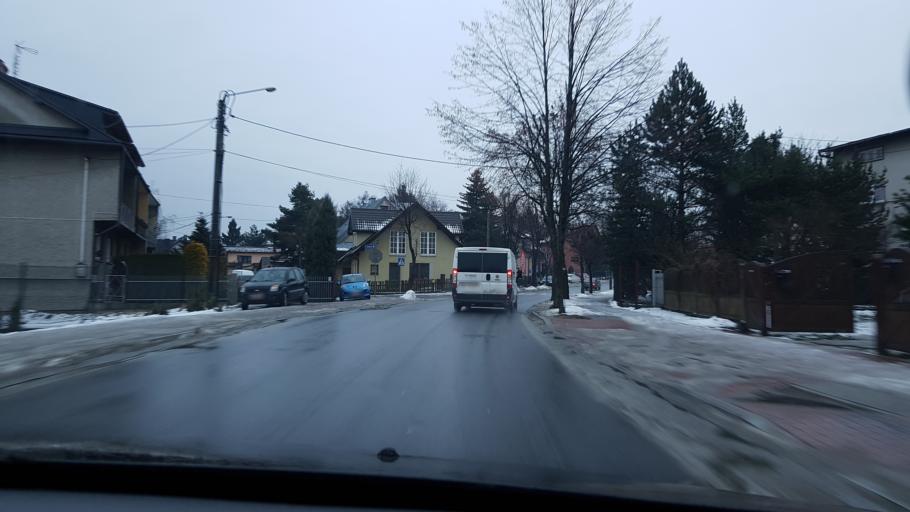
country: PL
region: Lesser Poland Voivodeship
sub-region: Powiat nowotarski
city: Nowy Targ
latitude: 49.4791
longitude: 20.0461
